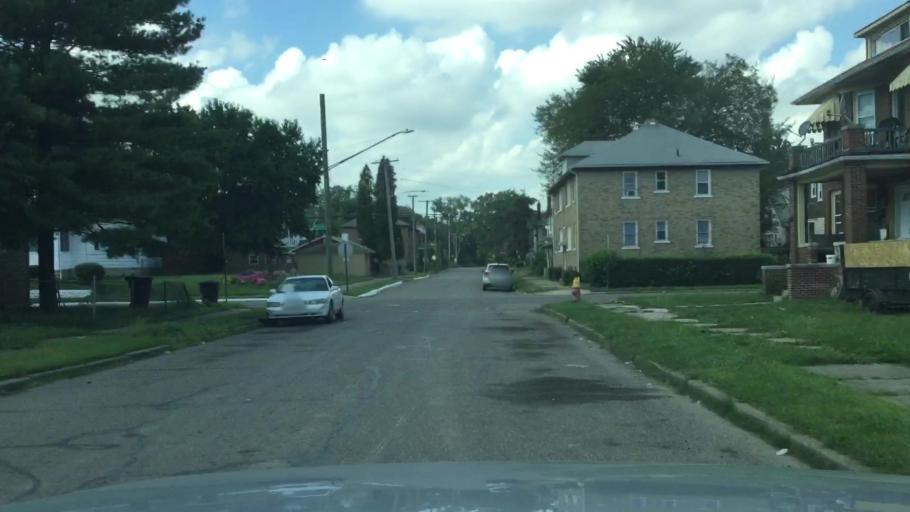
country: US
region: Michigan
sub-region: Wayne County
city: Dearborn
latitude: 42.3570
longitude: -83.1427
